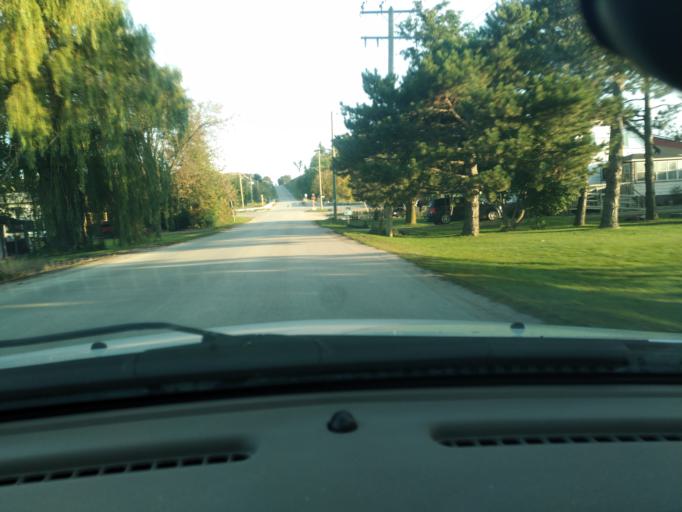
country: CA
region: Ontario
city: Bradford West Gwillimbury
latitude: 44.0428
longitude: -79.6242
